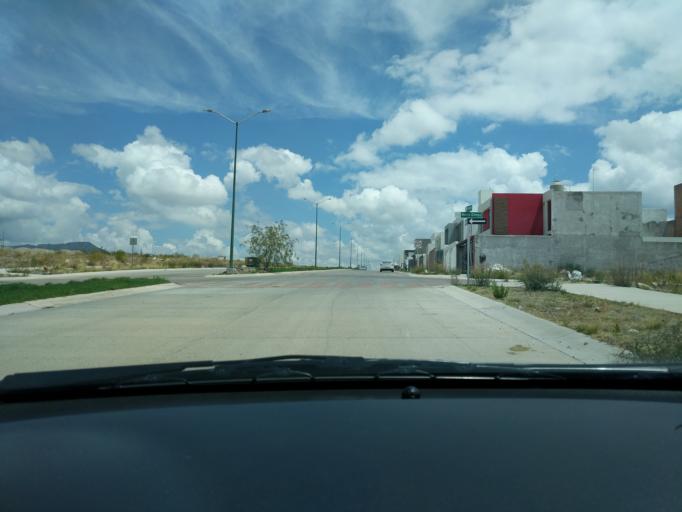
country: MX
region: San Luis Potosi
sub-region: Mexquitic de Carmona
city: Guadalupe Victoria
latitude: 22.1559
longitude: -101.0525
